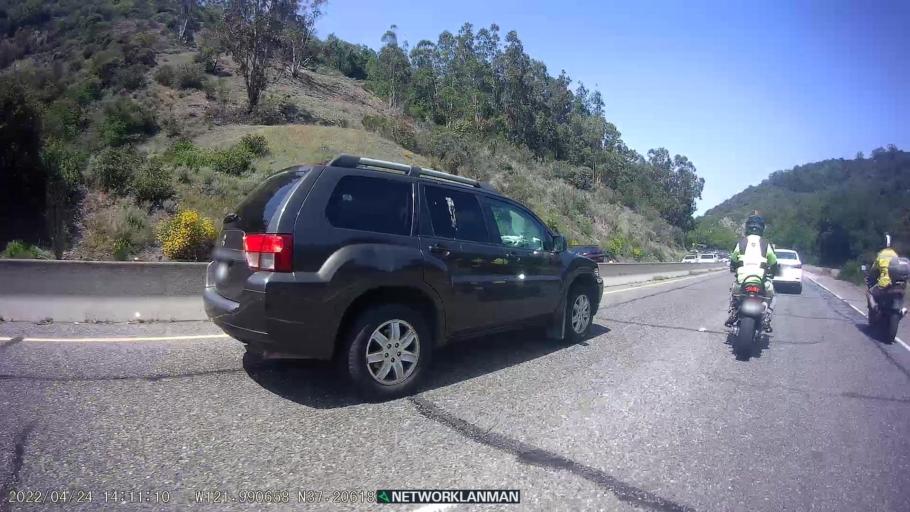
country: US
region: California
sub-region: Santa Clara County
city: Los Gatos
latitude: 37.2064
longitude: -121.9919
